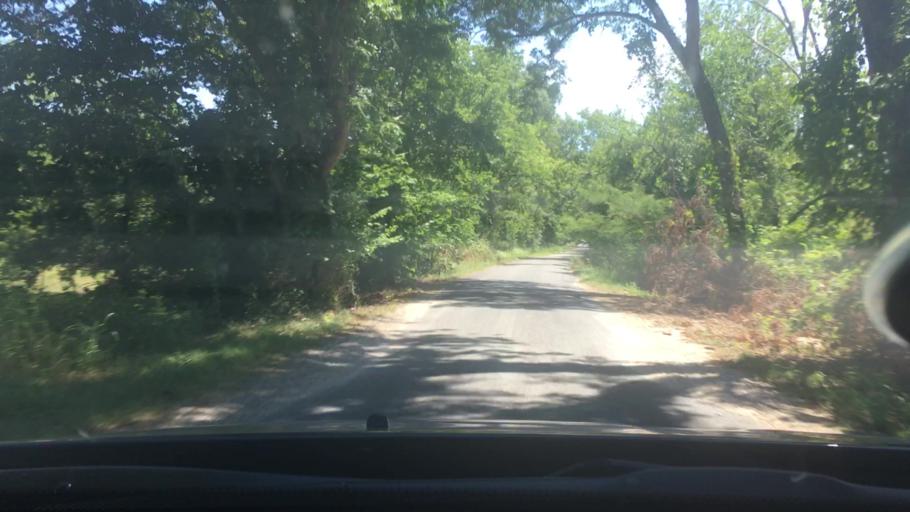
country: US
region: Oklahoma
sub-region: Bryan County
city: Durant
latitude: 33.9830
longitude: -96.2631
